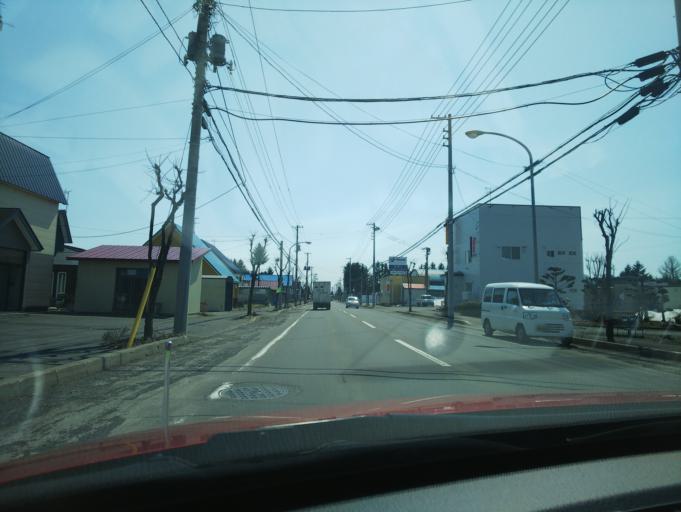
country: JP
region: Hokkaido
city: Nayoro
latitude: 44.3410
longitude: 142.4643
